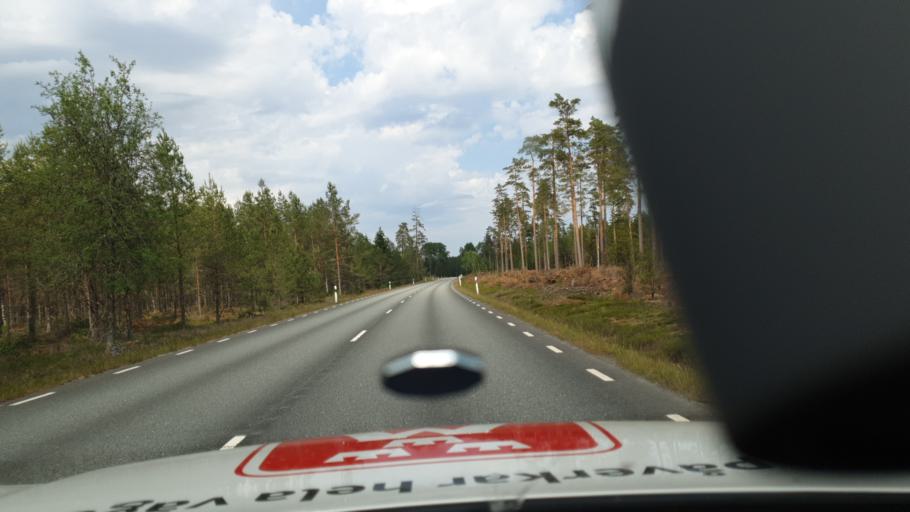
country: SE
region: Joenkoeping
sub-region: Varnamo Kommun
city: Varnamo
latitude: 57.2931
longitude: 14.0759
